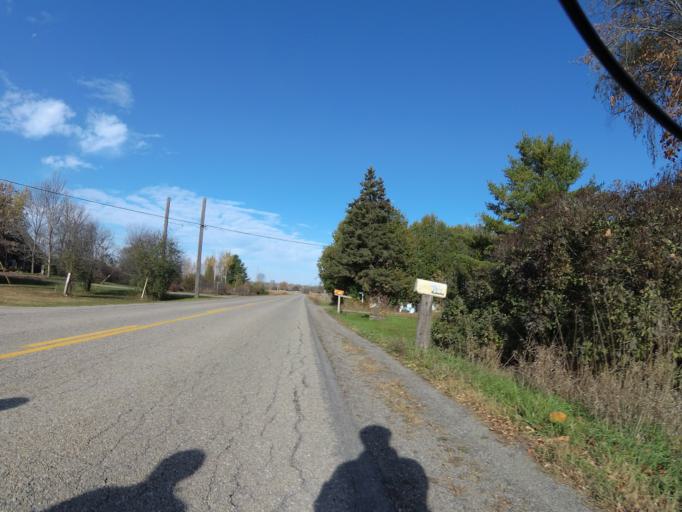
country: CA
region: Ontario
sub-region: Lanark County
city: Smiths Falls
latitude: 44.8252
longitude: -75.9423
